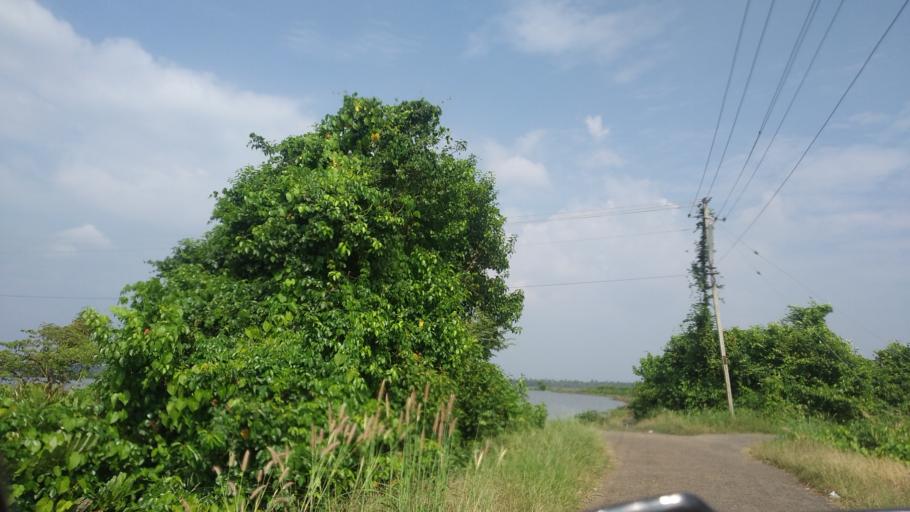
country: IN
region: Kerala
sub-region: Ernakulam
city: Elur
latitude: 10.0867
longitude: 76.2180
